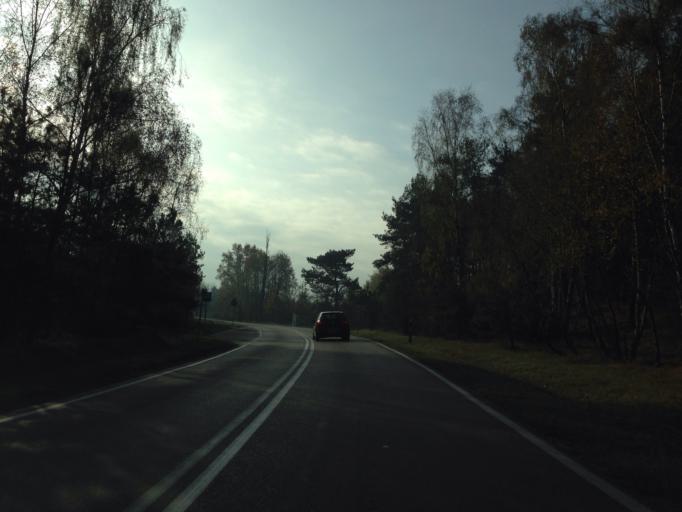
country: PL
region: Masovian Voivodeship
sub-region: Powiat zurominski
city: Biezun
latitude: 52.9309
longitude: 19.8846
